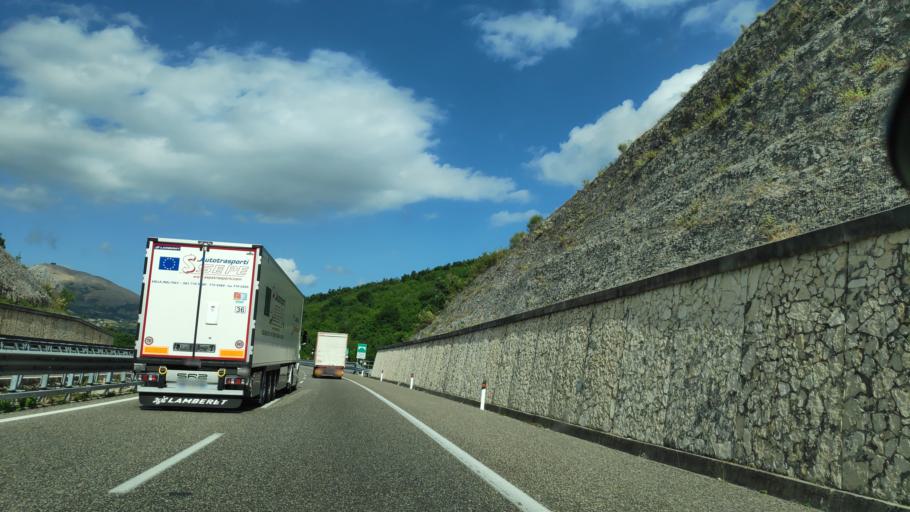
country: IT
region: Campania
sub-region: Provincia di Salerno
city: Pertosa
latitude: 40.5312
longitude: 15.4515
